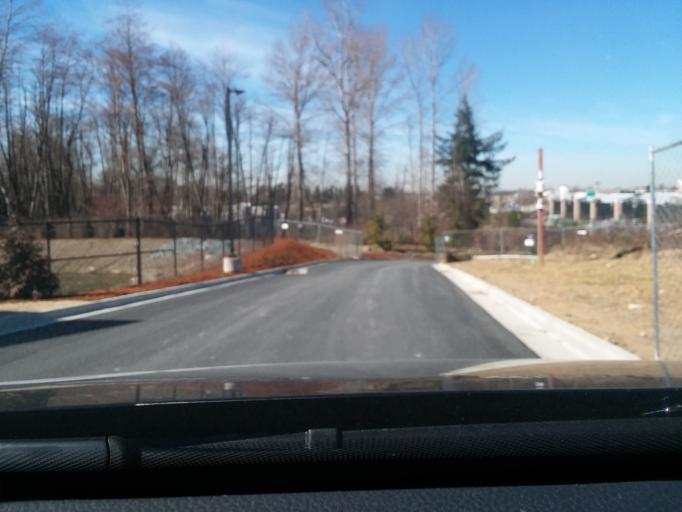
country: US
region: Washington
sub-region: Pierce County
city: South Hill
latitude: 47.1565
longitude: -122.2836
